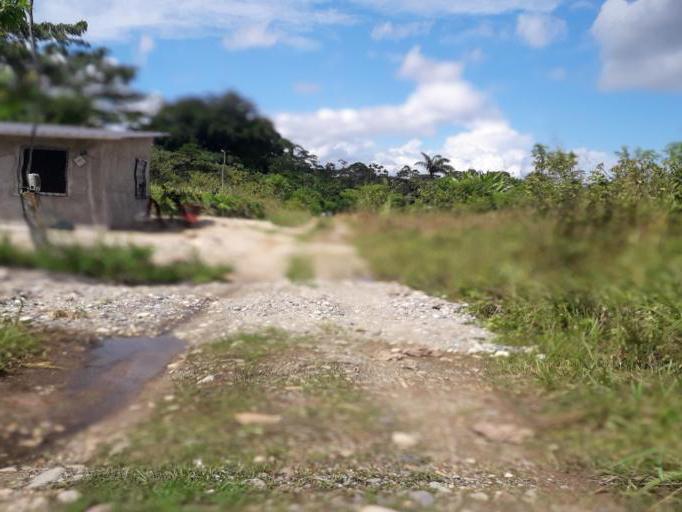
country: EC
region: Napo
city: Tena
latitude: -0.9584
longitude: -77.8172
